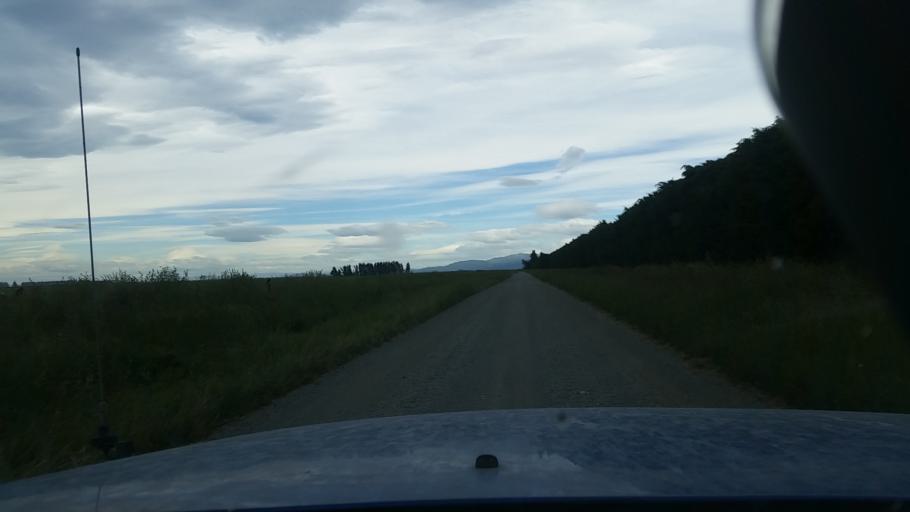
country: NZ
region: Canterbury
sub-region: Ashburton District
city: Methven
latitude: -43.7910
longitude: 171.5213
